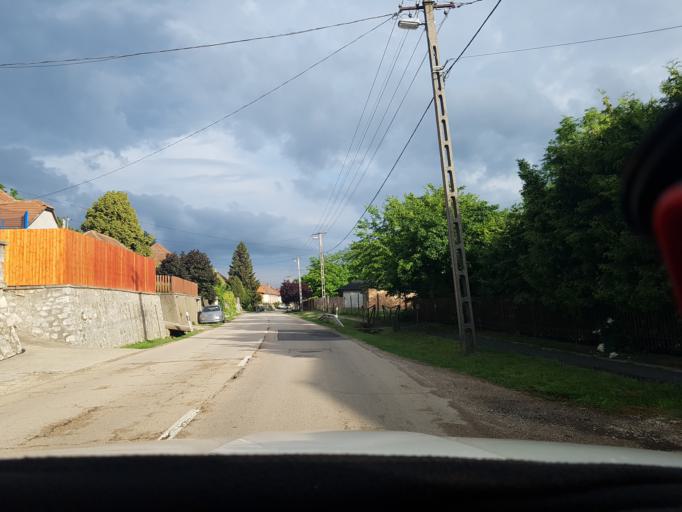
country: HU
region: Komarom-Esztergom
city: Sarisap
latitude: 47.6832
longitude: 18.6720
